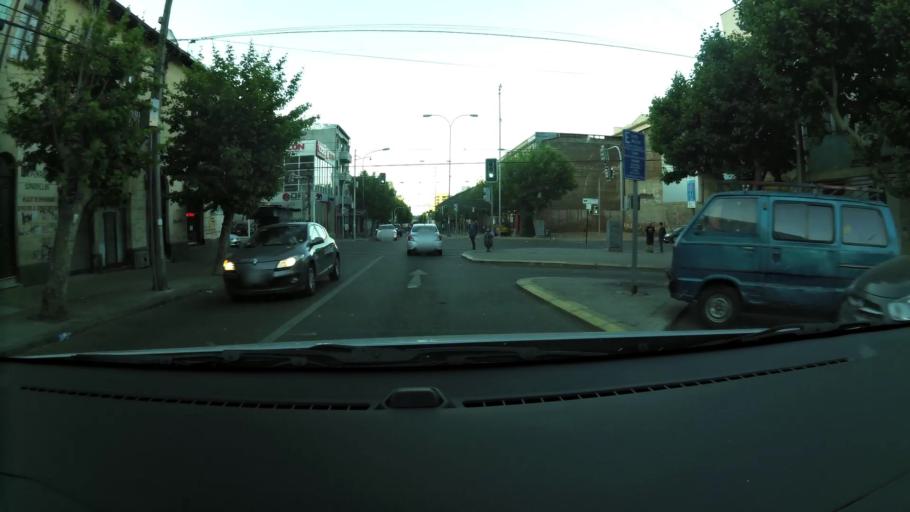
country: CL
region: Valparaiso
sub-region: Provincia de Valparaiso
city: Valparaiso
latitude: -33.0508
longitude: -71.6085
